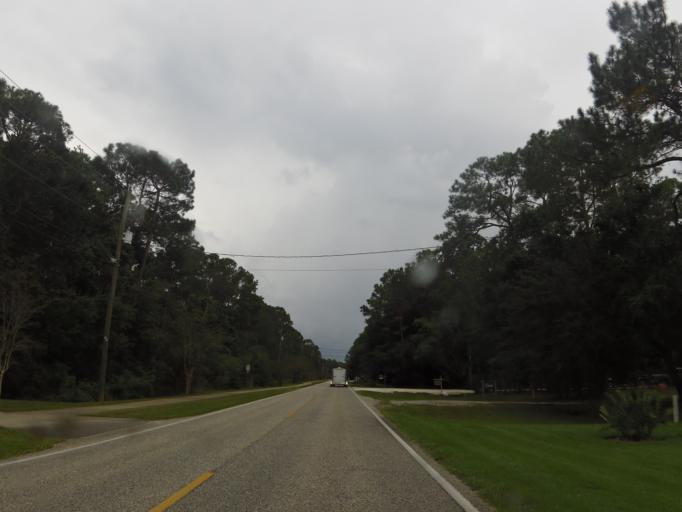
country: US
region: Alabama
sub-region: Baldwin County
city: Point Clear
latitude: 30.4507
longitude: -87.9141
